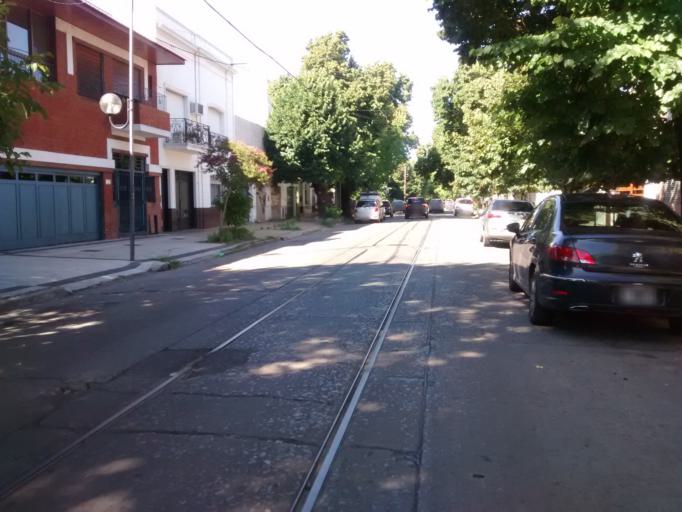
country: AR
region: Buenos Aires
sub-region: Partido de La Plata
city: La Plata
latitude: -34.9286
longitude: -57.9295
